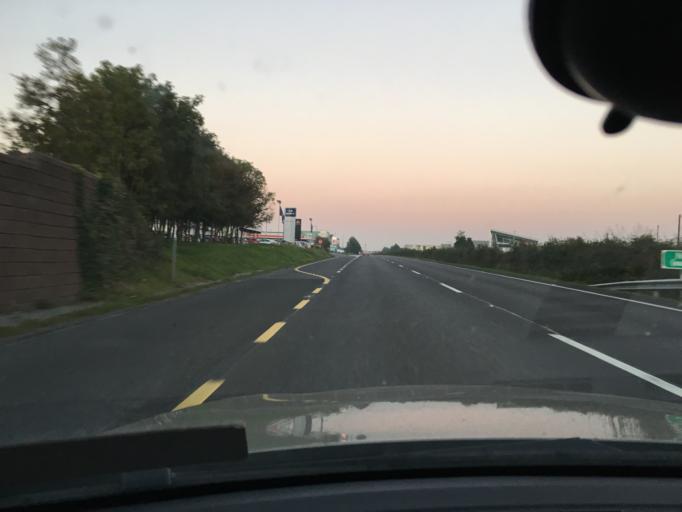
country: IE
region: Connaught
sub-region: County Galway
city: Gaillimh
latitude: 53.2892
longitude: -9.0099
